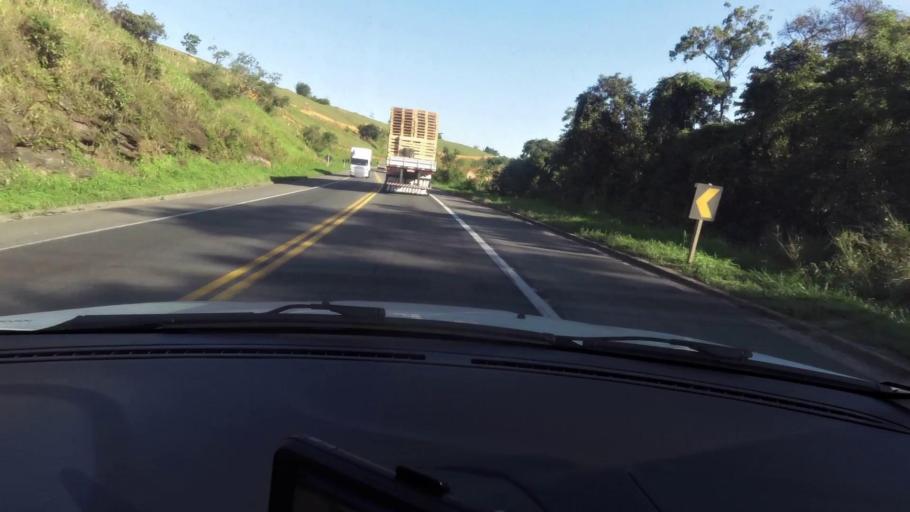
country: BR
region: Espirito Santo
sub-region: Alfredo Chaves
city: Alfredo Chaves
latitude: -20.6733
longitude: -40.6646
